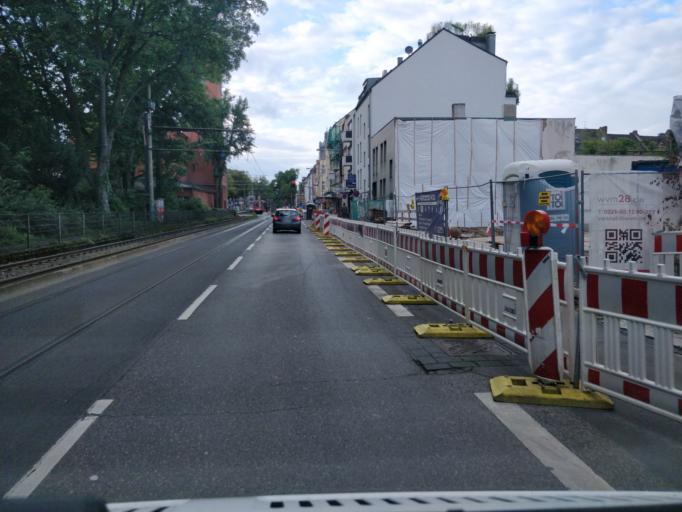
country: DE
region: North Rhine-Westphalia
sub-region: Regierungsbezirk Koln
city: Neustadt/Sued
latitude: 50.9229
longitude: 6.9132
